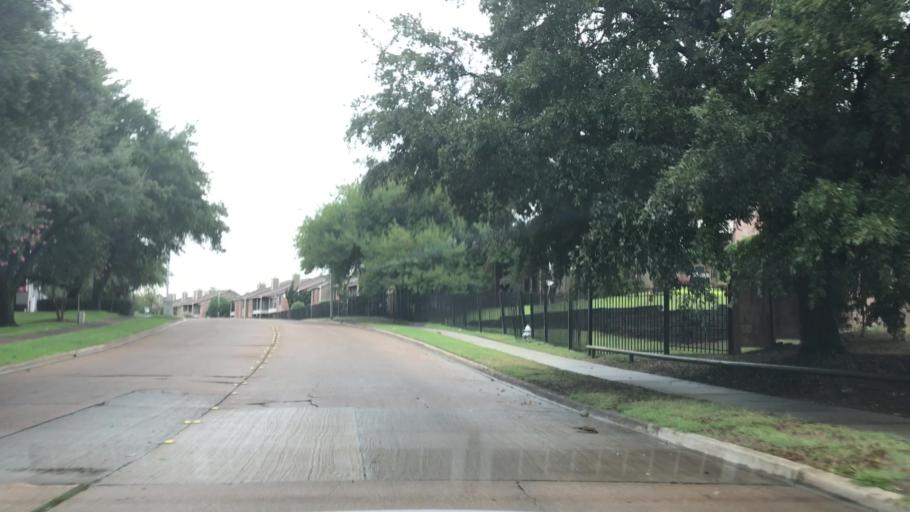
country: US
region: Texas
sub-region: Denton County
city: Lewisville
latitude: 33.0187
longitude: -96.9867
